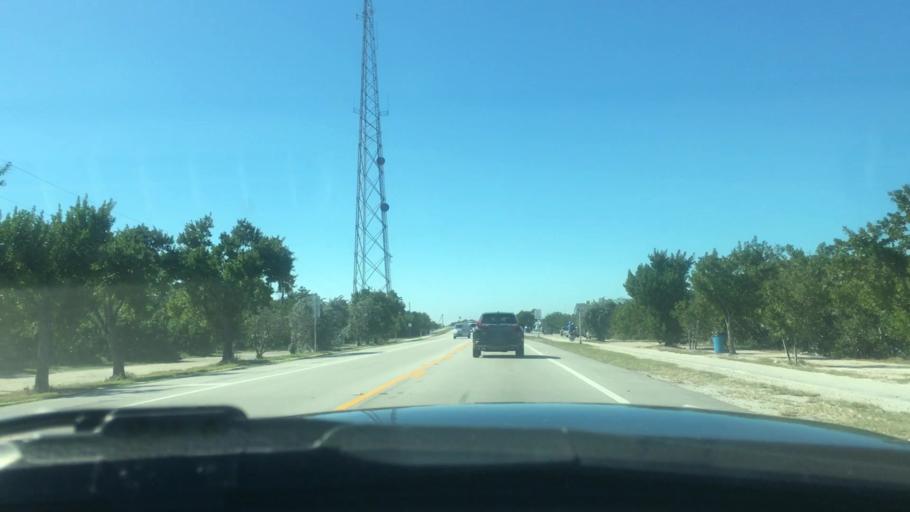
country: US
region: Florida
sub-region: Monroe County
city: Islamorada
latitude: 24.8967
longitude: -80.6623
